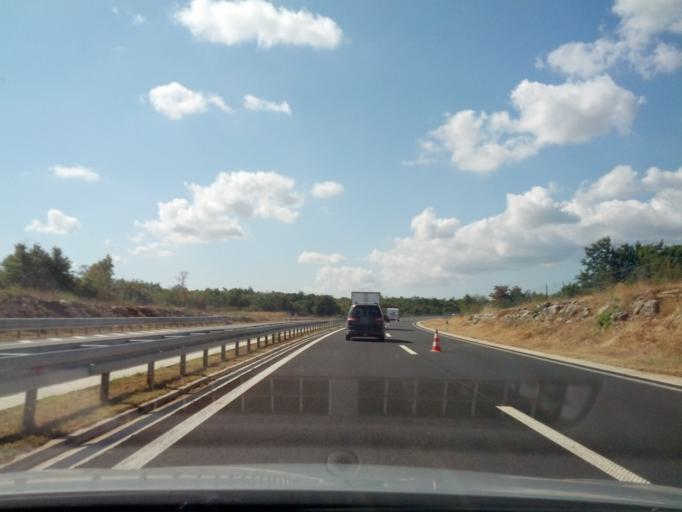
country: HR
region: Istarska
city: Vodnjan
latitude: 45.0218
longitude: 13.8417
